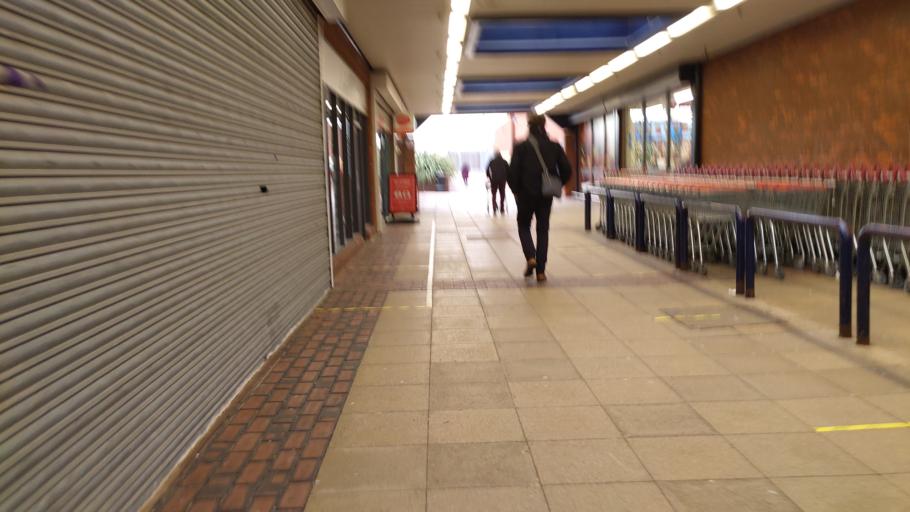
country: GB
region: England
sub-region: Hertfordshire
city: Potters Bar
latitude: 51.6976
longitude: -0.1926
